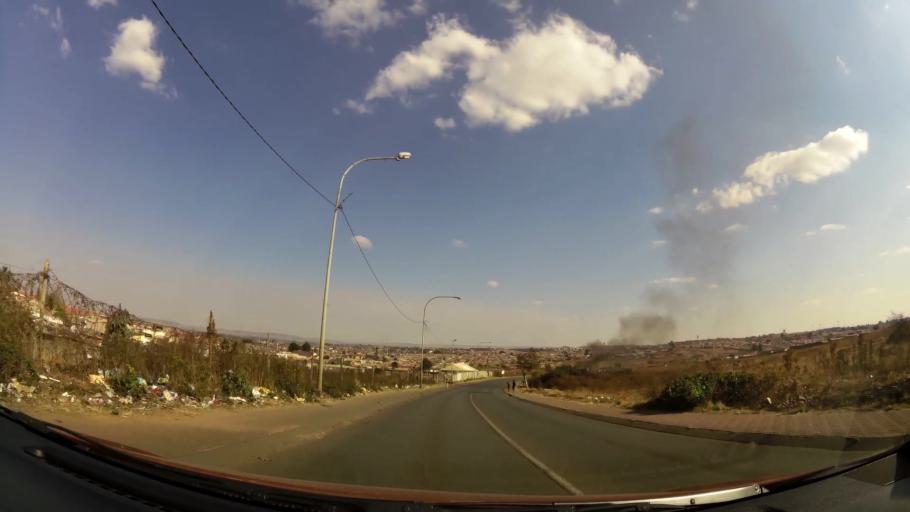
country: ZA
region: Gauteng
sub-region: City of Johannesburg Metropolitan Municipality
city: Soweto
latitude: -26.2226
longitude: 27.8886
